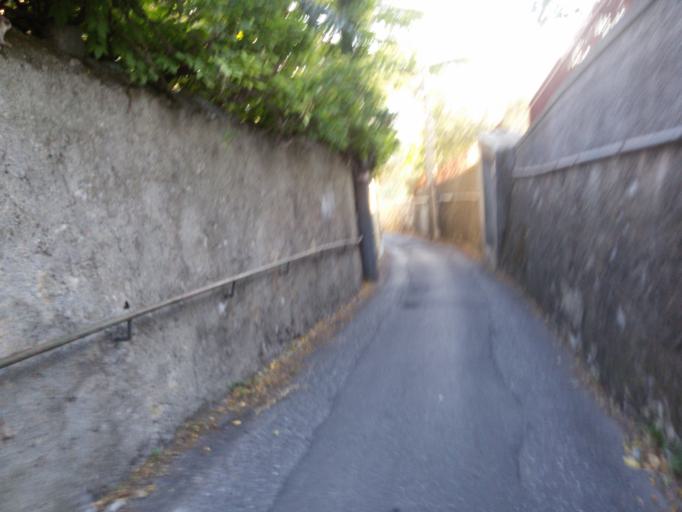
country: IT
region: Liguria
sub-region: Provincia di Genova
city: Genoa
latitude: 44.4119
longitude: 8.9778
